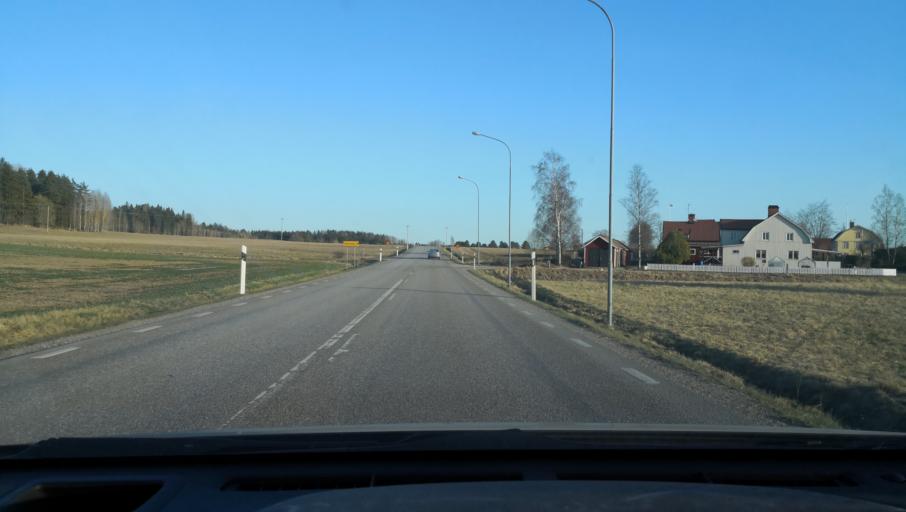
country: SE
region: Uppsala
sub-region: Heby Kommun
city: Heby
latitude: 59.9334
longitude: 16.8705
